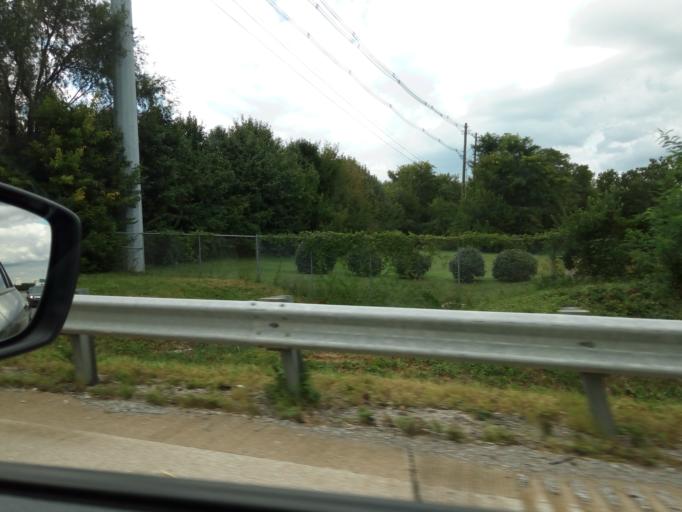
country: US
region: Kentucky
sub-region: Jefferson County
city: Saint Regis Park
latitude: 38.2337
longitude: -85.6270
